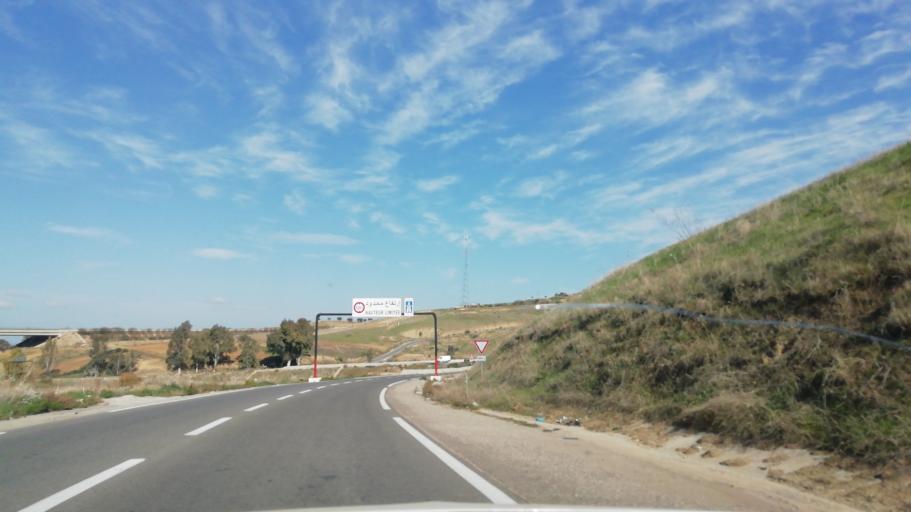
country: DZ
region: Tlemcen
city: Chetouane
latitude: 34.9792
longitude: -1.2388
